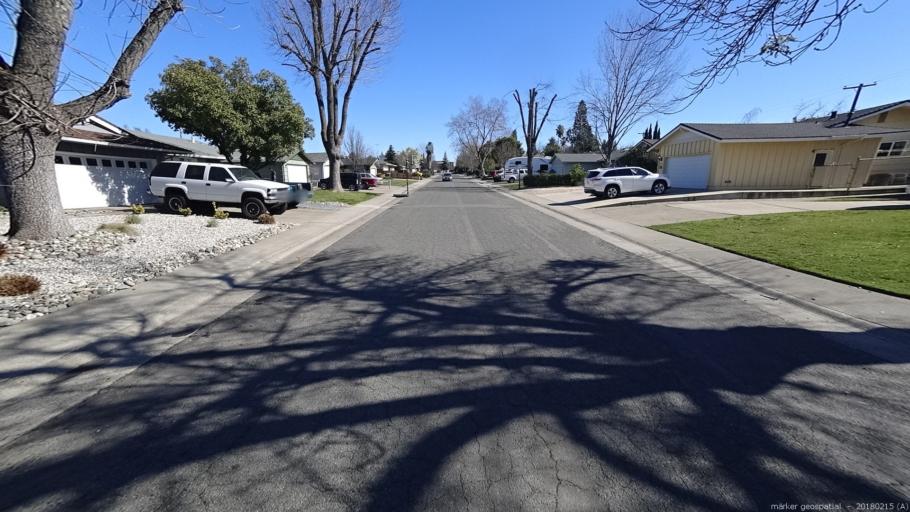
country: US
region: California
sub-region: Sacramento County
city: Foothill Farms
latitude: 38.6672
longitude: -121.3140
